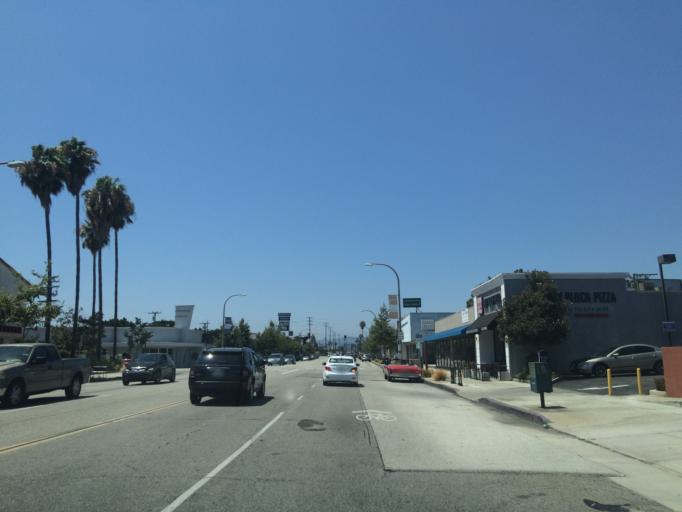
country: US
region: California
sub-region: Los Angeles County
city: Culver City
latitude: 34.0030
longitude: -118.4068
